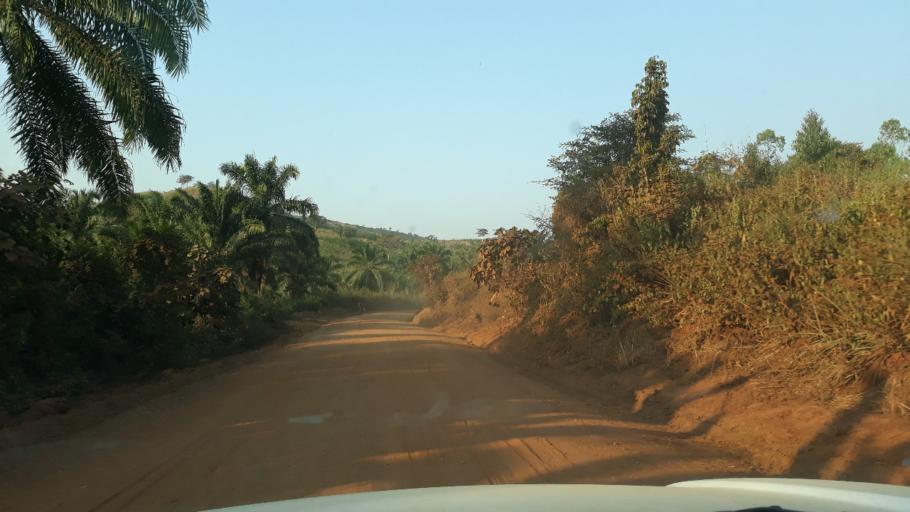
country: BI
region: Bururi
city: Rumonge
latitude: -4.2051
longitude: 29.0066
